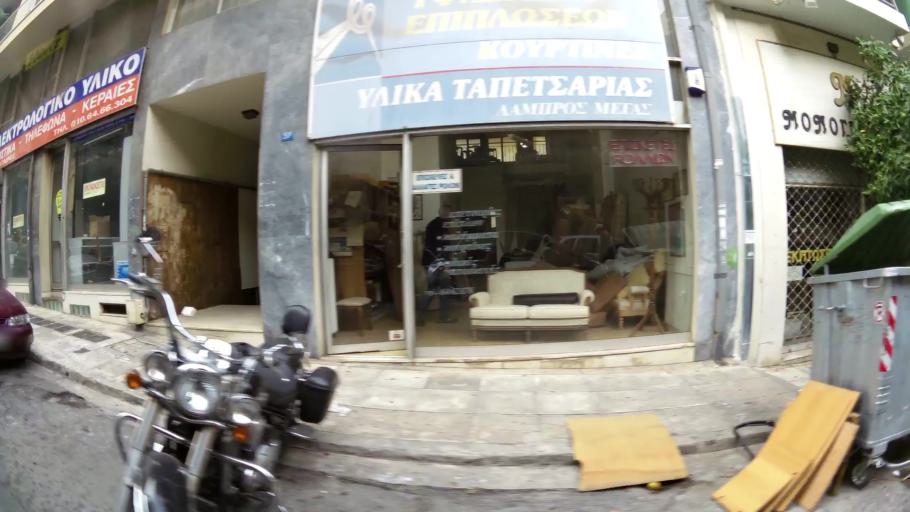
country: GR
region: Attica
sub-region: Nomarchia Athinas
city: Kipseli
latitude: 37.9923
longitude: 23.7465
